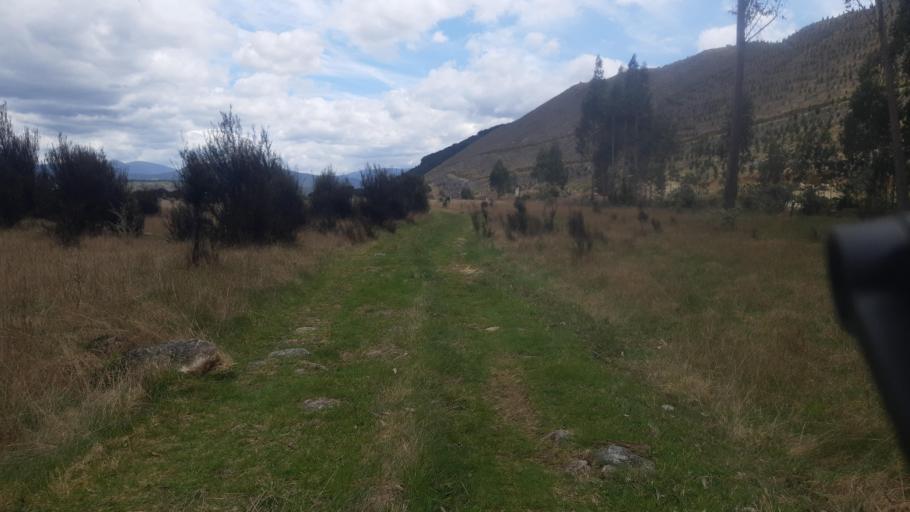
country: NZ
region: Tasman
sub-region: Tasman District
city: Wakefield
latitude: -41.7699
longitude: 172.7978
